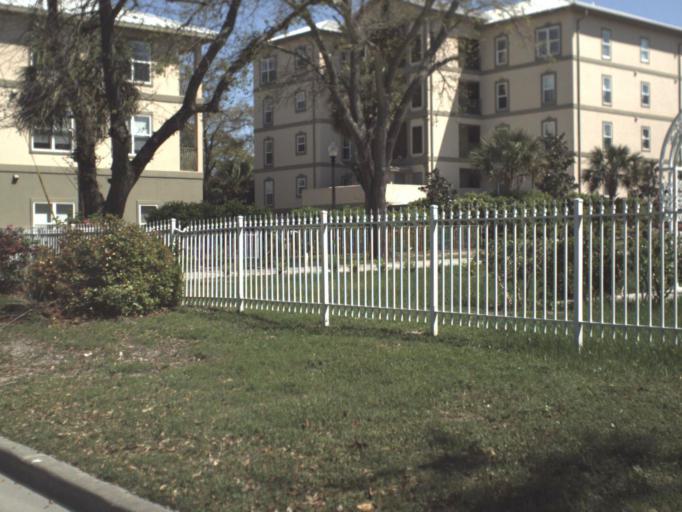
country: US
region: Florida
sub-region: Okaloosa County
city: Fort Walton Beach
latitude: 30.4028
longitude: -86.6037
